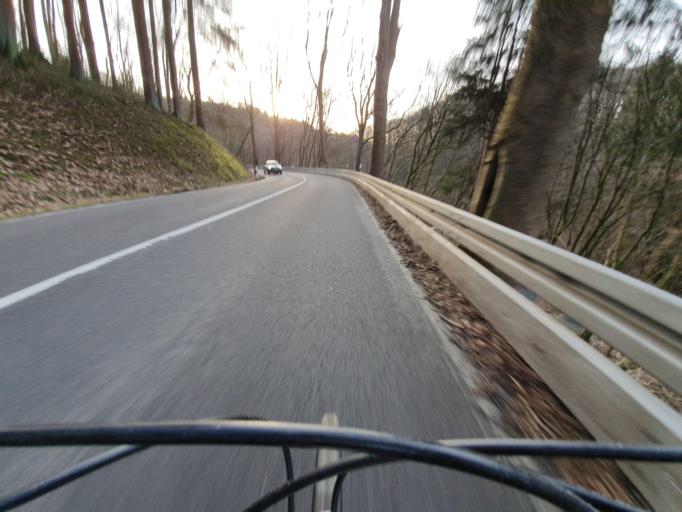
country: DE
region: North Rhine-Westphalia
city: Burscheid
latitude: 51.0898
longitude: 7.1761
